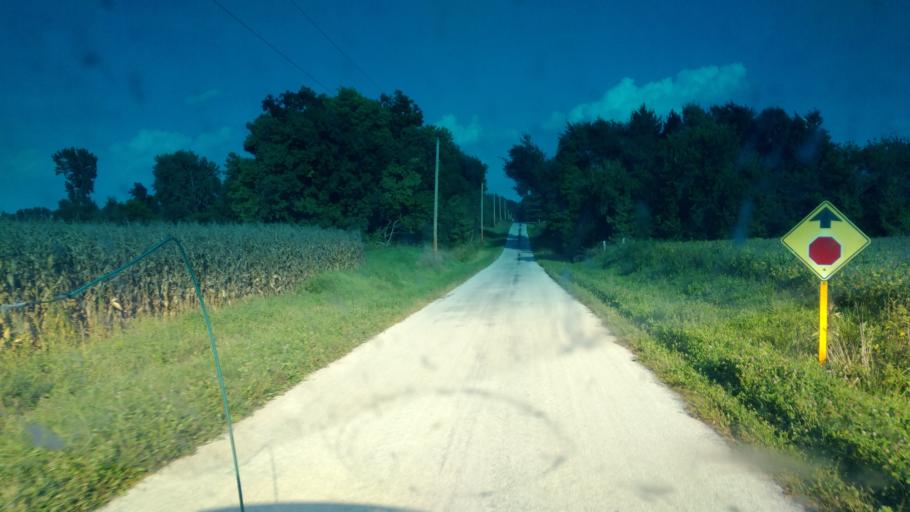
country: US
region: Ohio
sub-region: Wyandot County
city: Upper Sandusky
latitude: 40.9060
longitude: -83.2256
